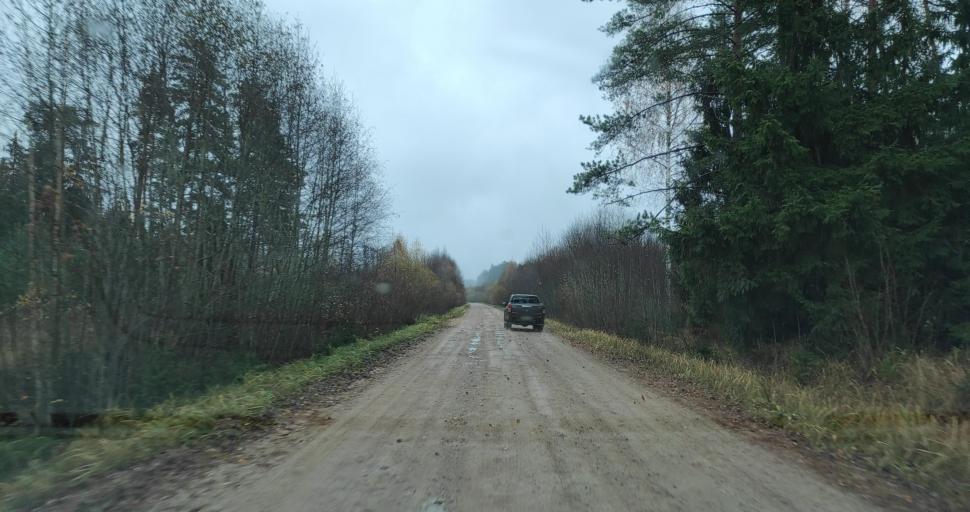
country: LV
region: Skrunda
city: Skrunda
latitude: 56.6924
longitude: 22.0930
